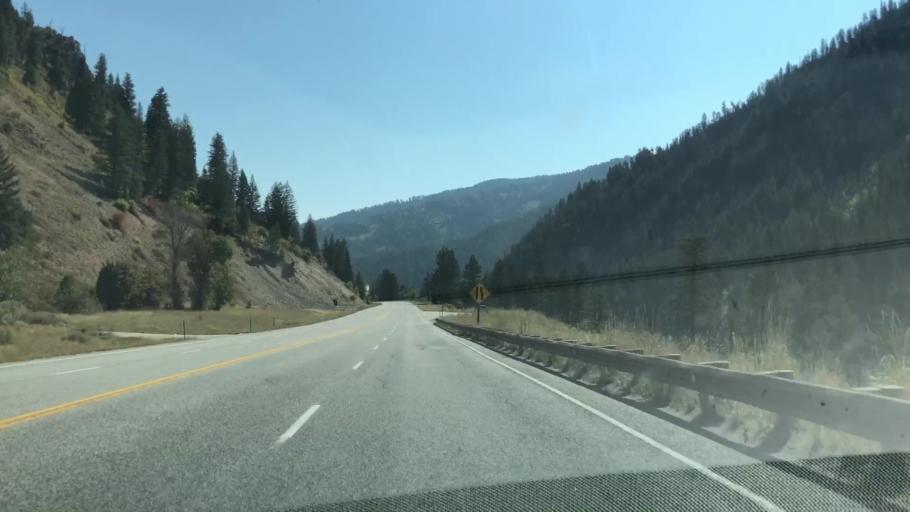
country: US
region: Wyoming
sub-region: Teton County
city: Hoback
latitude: 43.1972
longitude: -110.8924
